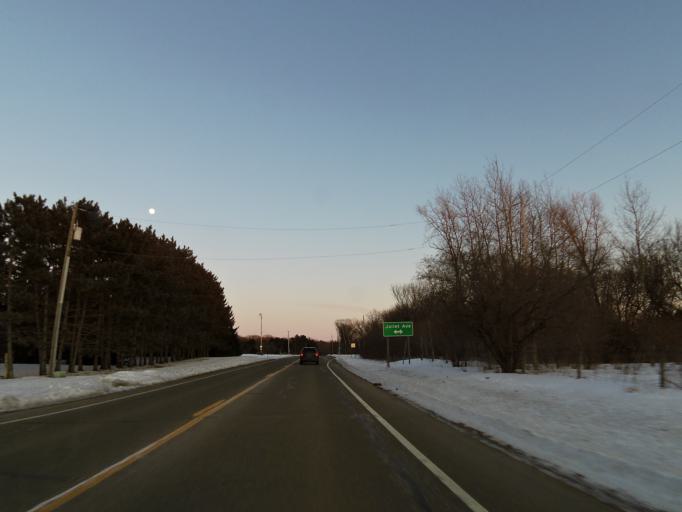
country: US
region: Minnesota
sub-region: Washington County
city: Grant
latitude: 45.0835
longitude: -92.9113
